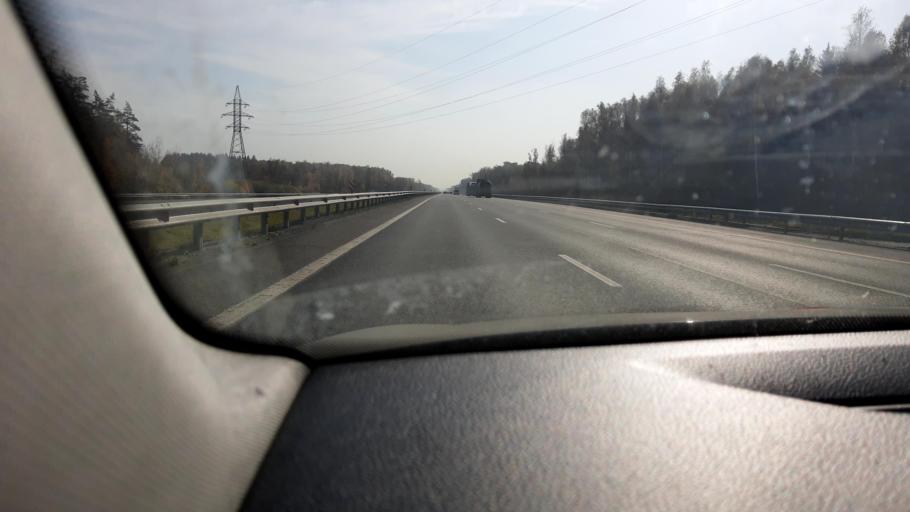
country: RU
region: Moskovskaya
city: Zhilevo
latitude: 54.9540
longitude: 37.9824
